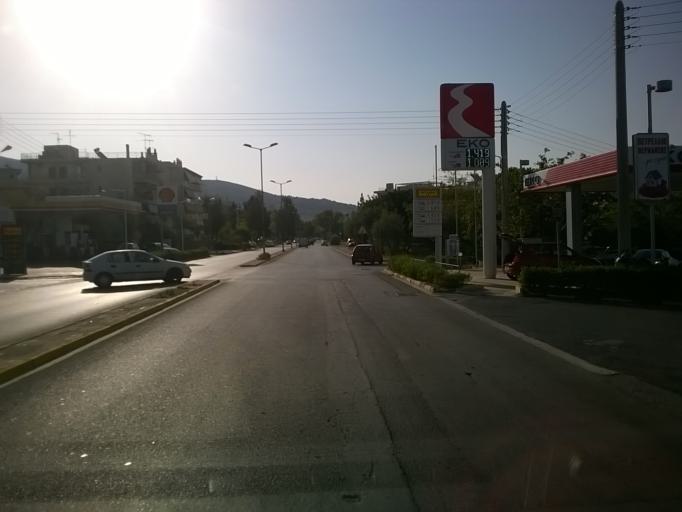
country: GR
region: Attica
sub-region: Nomarchia Athinas
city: Elliniko
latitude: 37.8832
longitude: 23.7540
